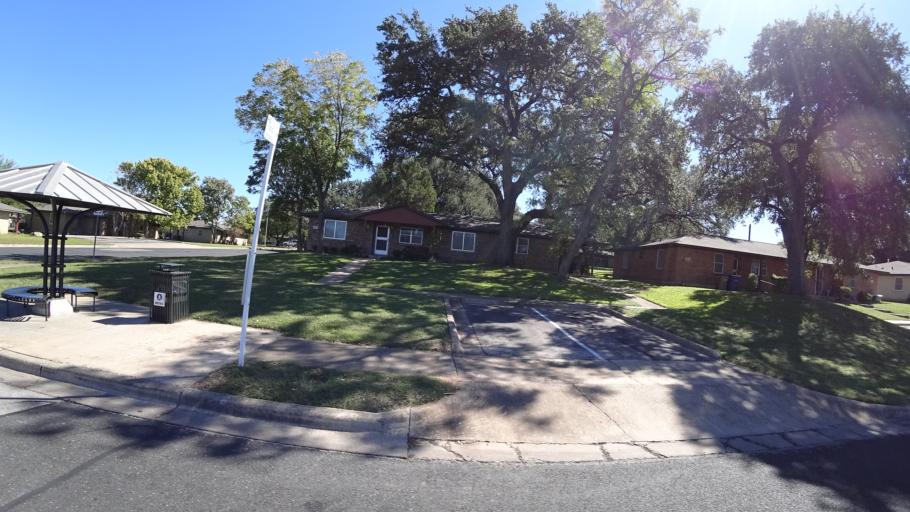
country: US
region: Texas
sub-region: Travis County
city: Austin
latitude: 30.2399
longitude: -97.7691
